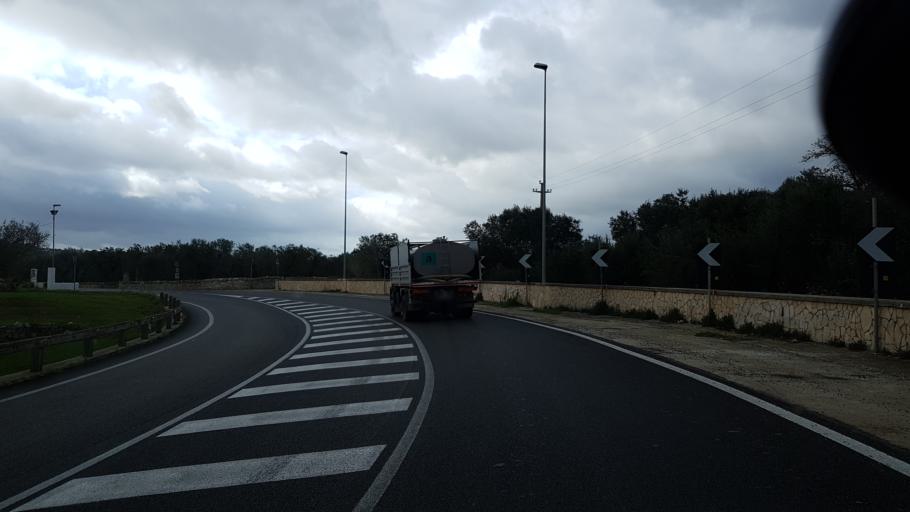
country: IT
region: Apulia
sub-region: Provincia di Bari
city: Alberobello
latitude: 40.7790
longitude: 17.2569
